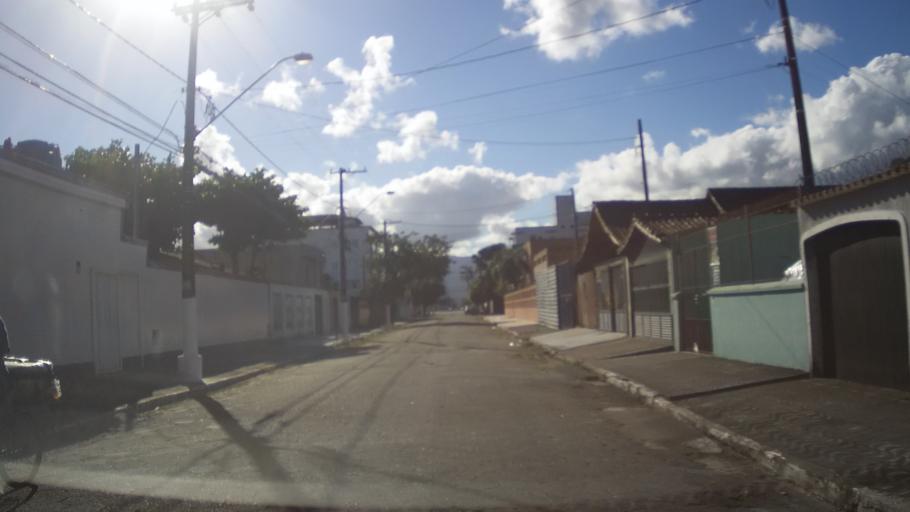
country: BR
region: Sao Paulo
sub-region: Praia Grande
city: Praia Grande
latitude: -24.0290
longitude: -46.4832
